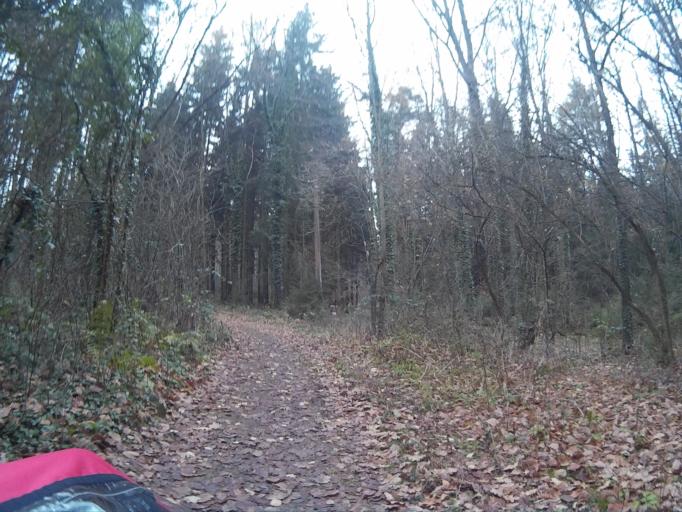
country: CZ
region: Plzensky
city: Stary Plzenec
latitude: 49.6820
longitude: 13.4782
